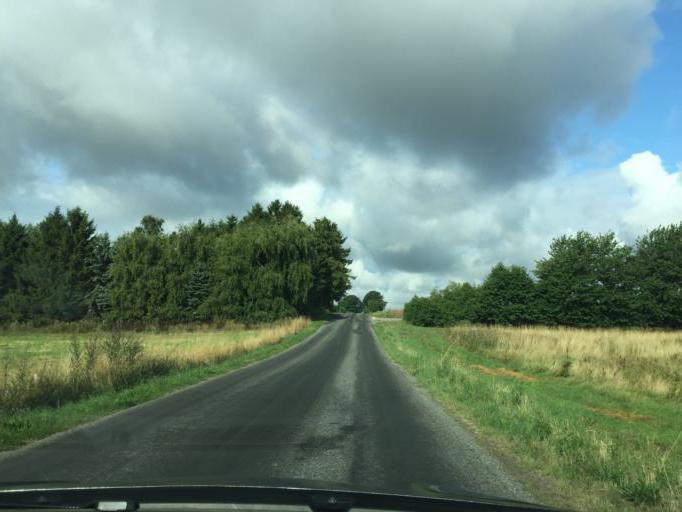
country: DK
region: South Denmark
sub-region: Faaborg-Midtfyn Kommune
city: Faaborg
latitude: 55.1924
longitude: 10.2324
